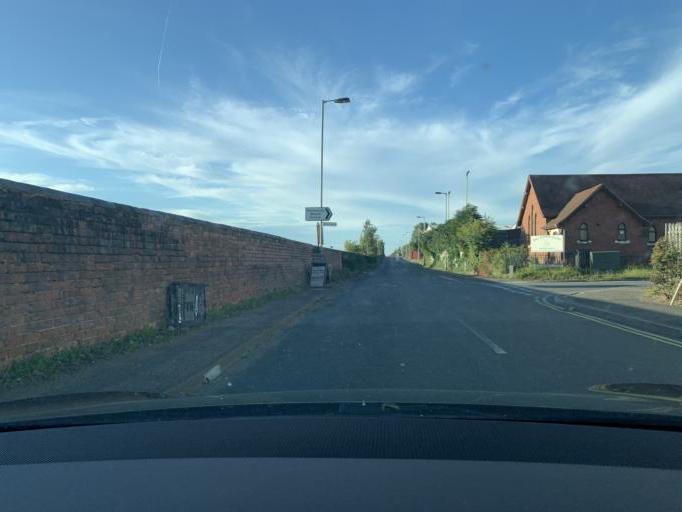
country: GB
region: England
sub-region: Staffordshire
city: Stafford
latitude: 52.8232
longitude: -2.1177
